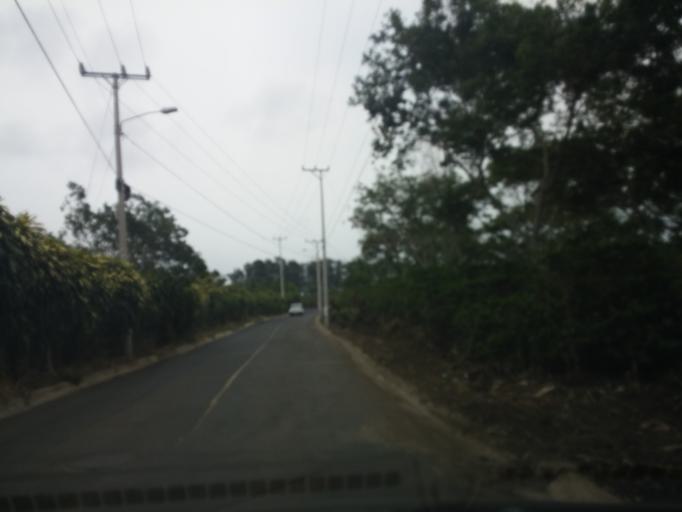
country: CR
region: Heredia
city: Llorente
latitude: 9.9842
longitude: -84.1471
